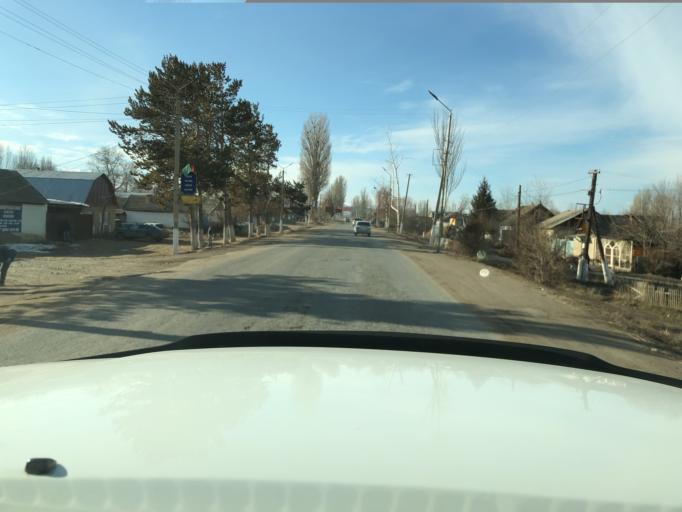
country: KG
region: Ysyk-Koel
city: Pokrovka
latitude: 42.3380
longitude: 77.9956
